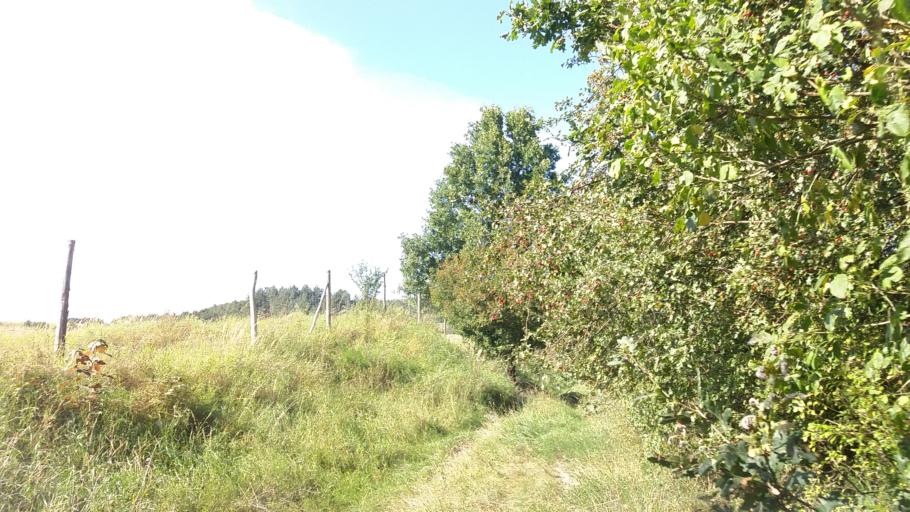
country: PL
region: West Pomeranian Voivodeship
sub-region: Powiat choszczenski
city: Krzecin
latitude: 53.1259
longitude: 15.5018
